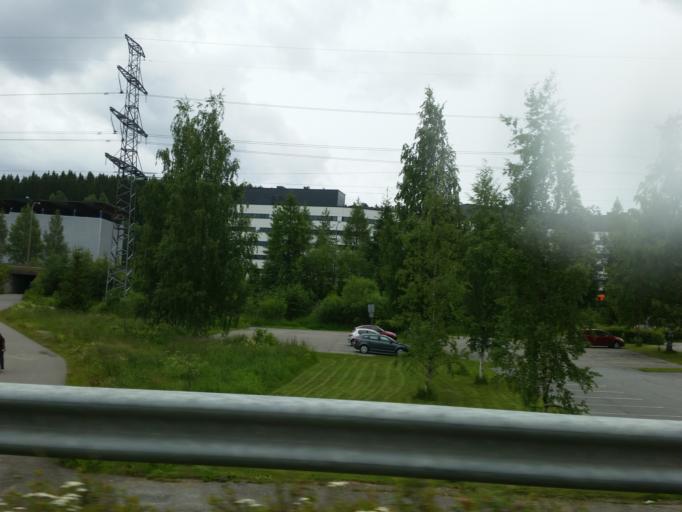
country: FI
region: Northern Savo
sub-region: Kuopio
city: Kuopio
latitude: 62.8920
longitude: 27.6381
